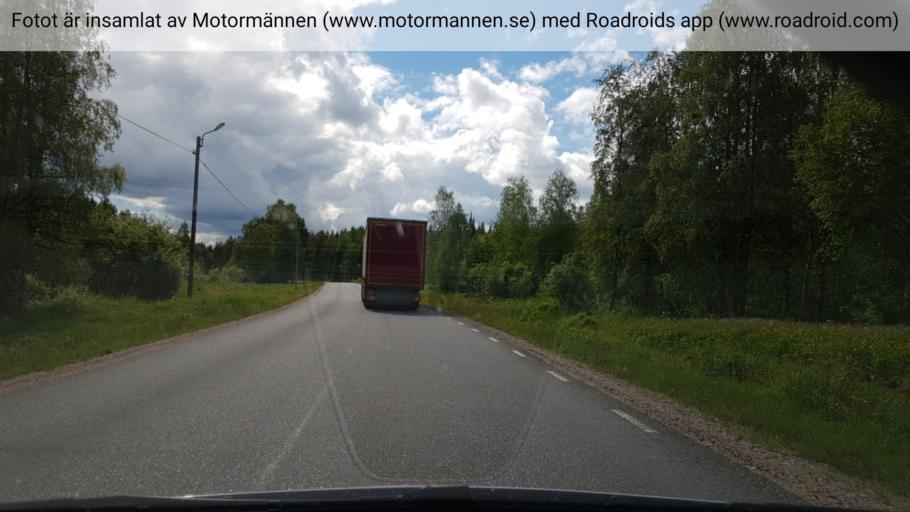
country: FI
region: Lapland
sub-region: Torniolaakso
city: Ylitornio
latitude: 66.2638
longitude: 23.6509
